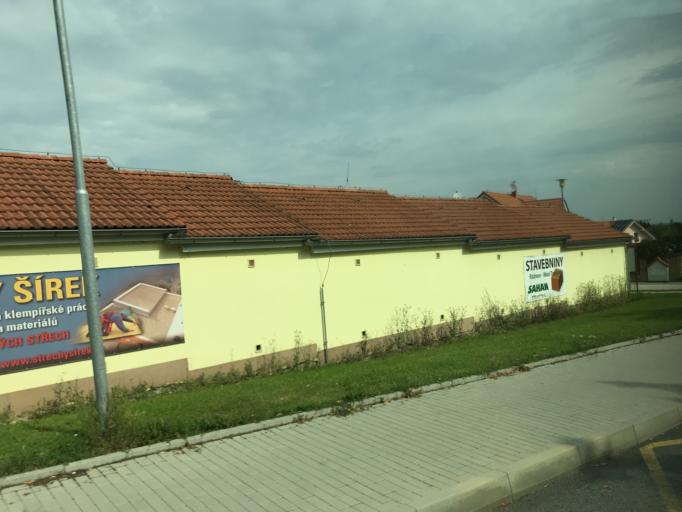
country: CZ
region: Jihocesky
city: Vcelna
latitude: 48.9294
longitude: 14.4573
